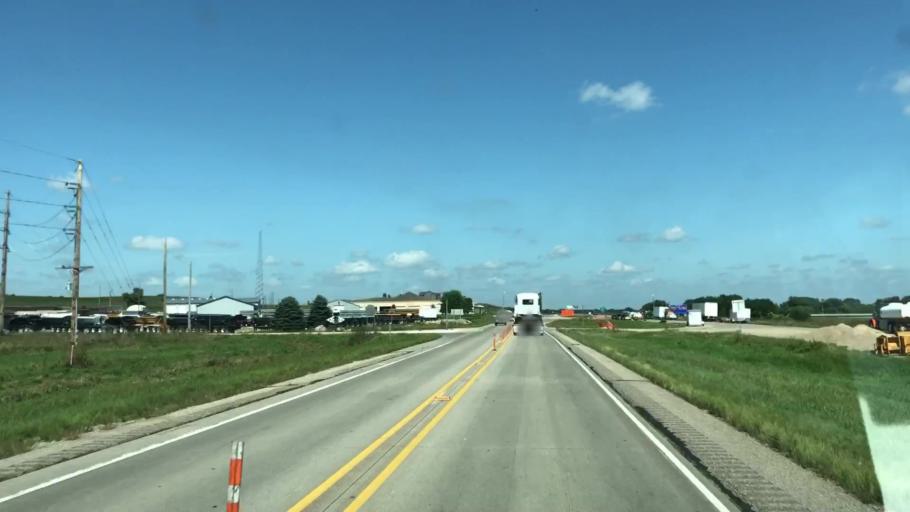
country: US
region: Iowa
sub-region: Plymouth County
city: Le Mars
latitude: 42.7453
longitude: -96.2135
